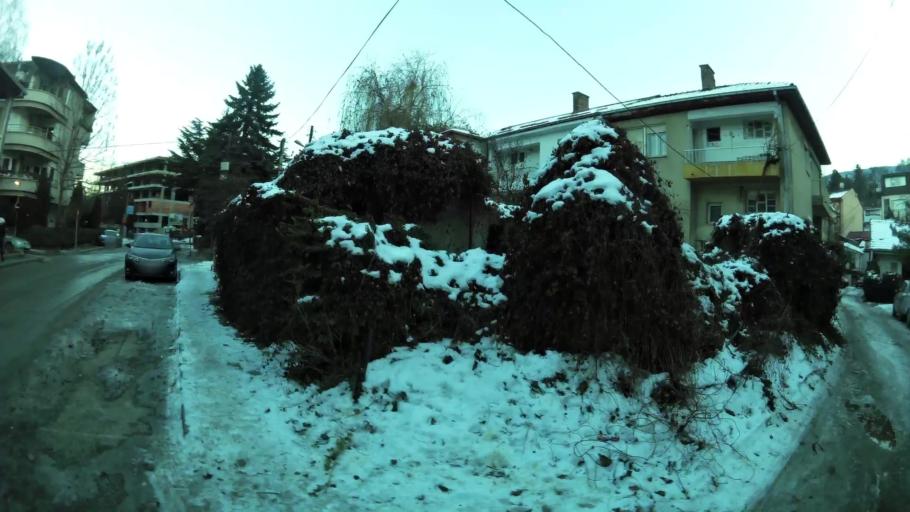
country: MK
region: Karpos
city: Skopje
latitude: 41.9904
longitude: 21.4152
